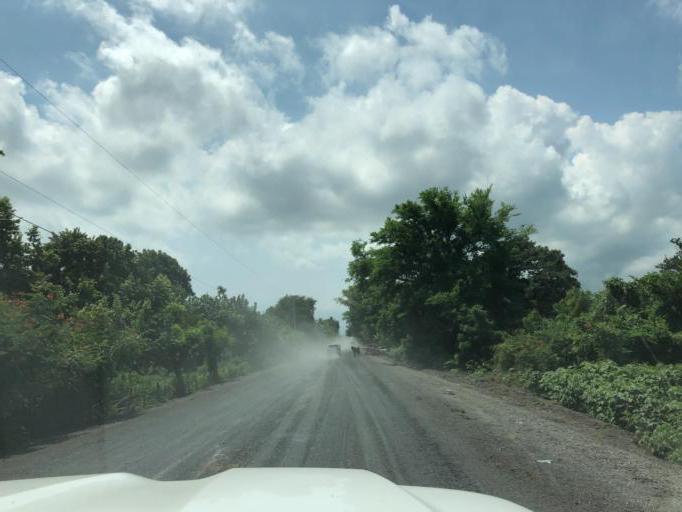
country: NI
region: Masaya
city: Tisma
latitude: 12.0483
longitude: -85.9176
